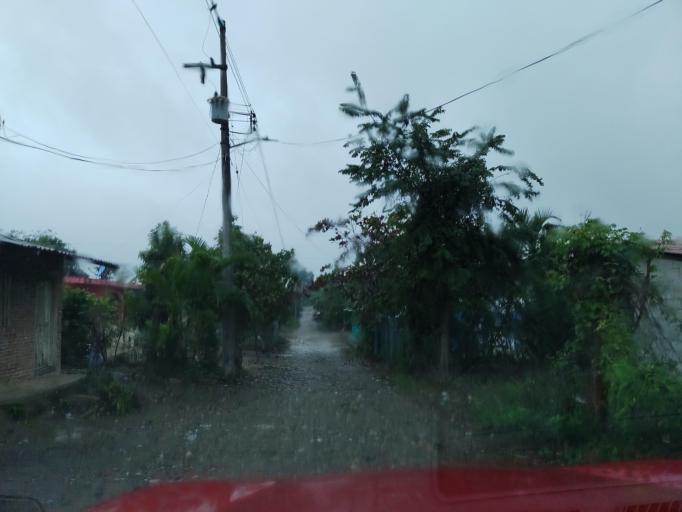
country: MX
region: Veracruz
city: Agua Dulce
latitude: 20.3363
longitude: -97.3155
